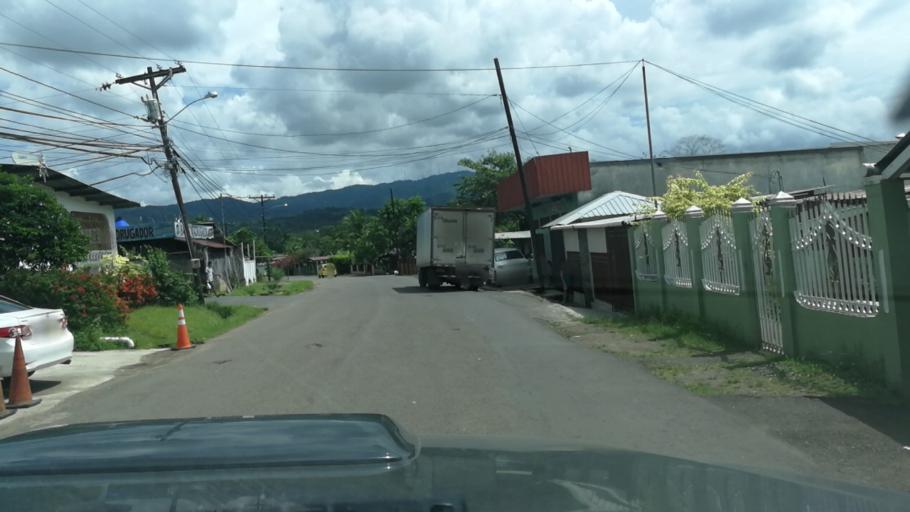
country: PA
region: Panama
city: Tocumen
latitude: 9.1010
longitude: -79.4112
